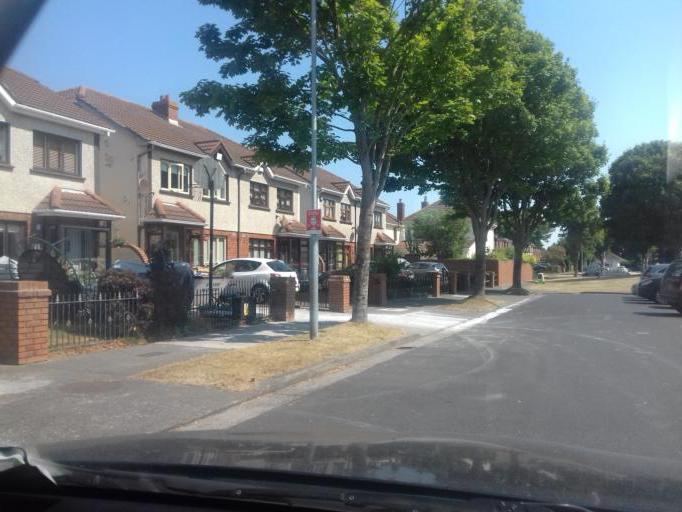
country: IE
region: Leinster
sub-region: Fingal County
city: Baldoyle
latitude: 53.3942
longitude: -6.1279
